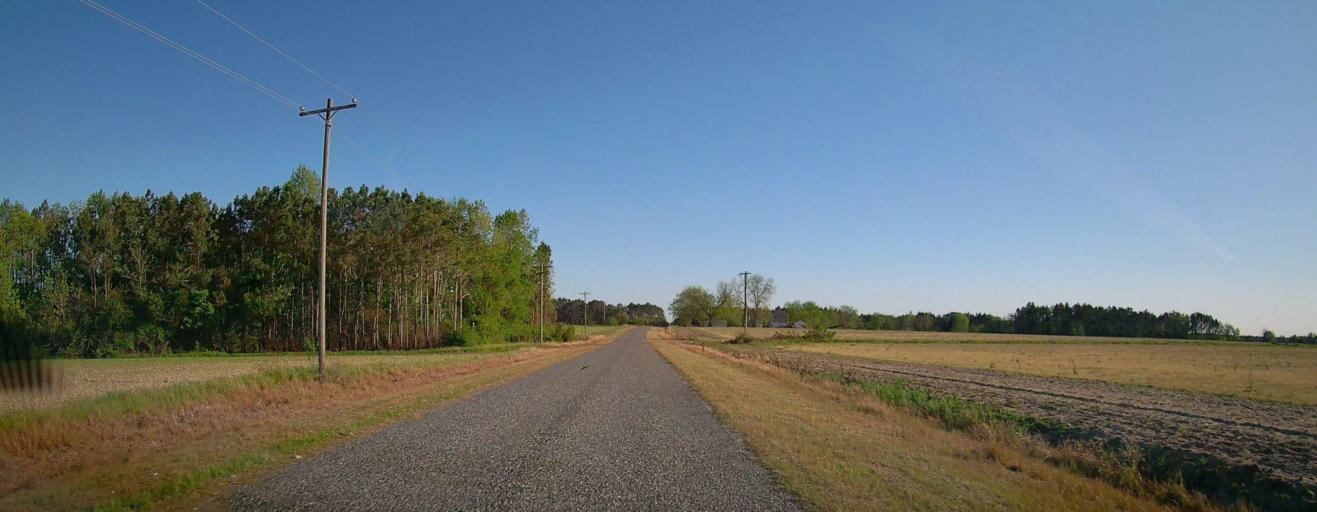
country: US
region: Georgia
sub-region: Ben Hill County
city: Fitzgerald
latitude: 31.6662
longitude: -83.1468
